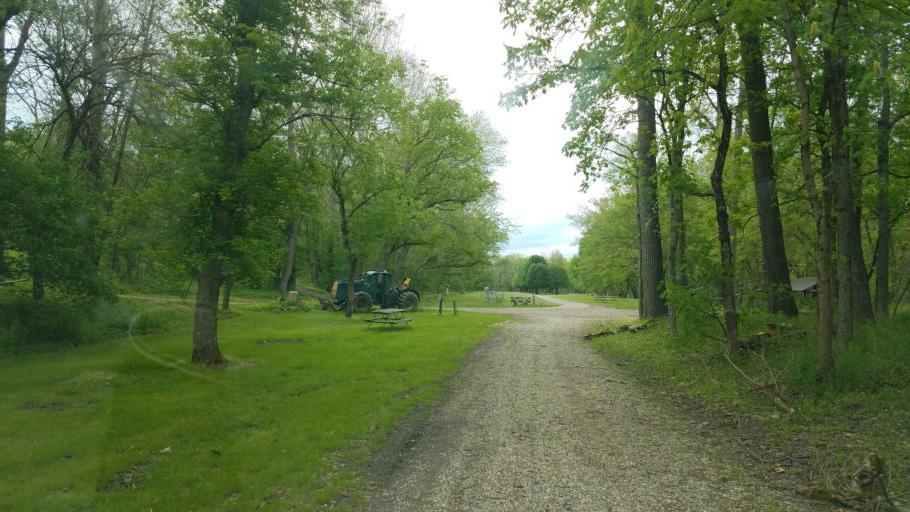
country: US
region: Ohio
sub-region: Ashland County
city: Loudonville
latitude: 40.5556
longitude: -82.1983
